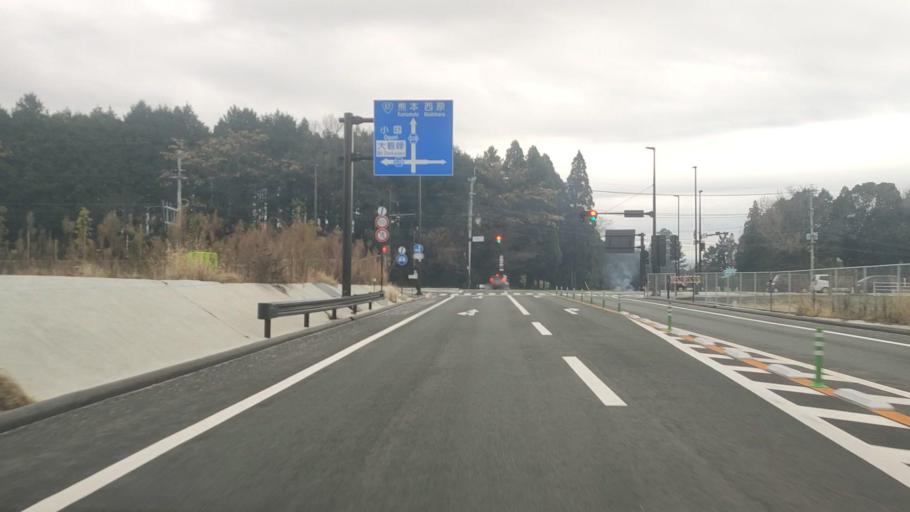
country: JP
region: Kumamoto
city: Ozu
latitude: 32.8883
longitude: 130.8966
